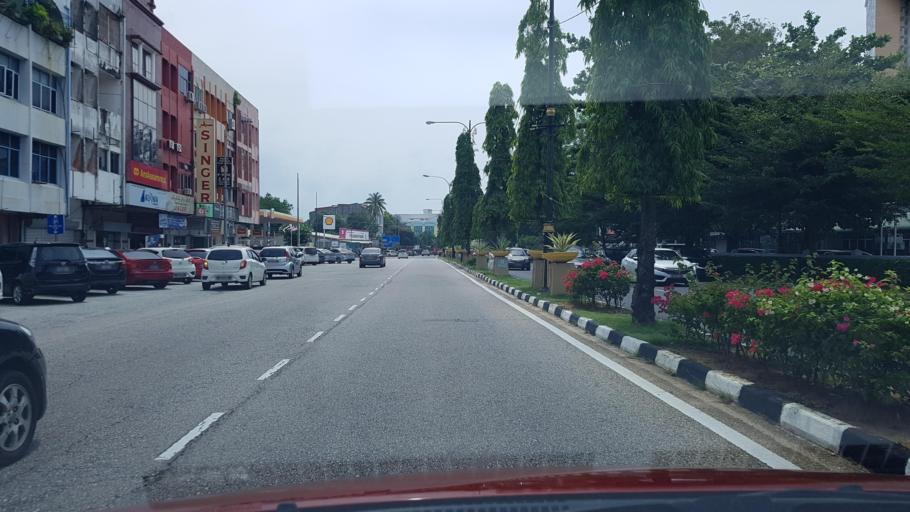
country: MY
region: Terengganu
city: Kuala Terengganu
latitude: 5.3262
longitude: 103.1482
